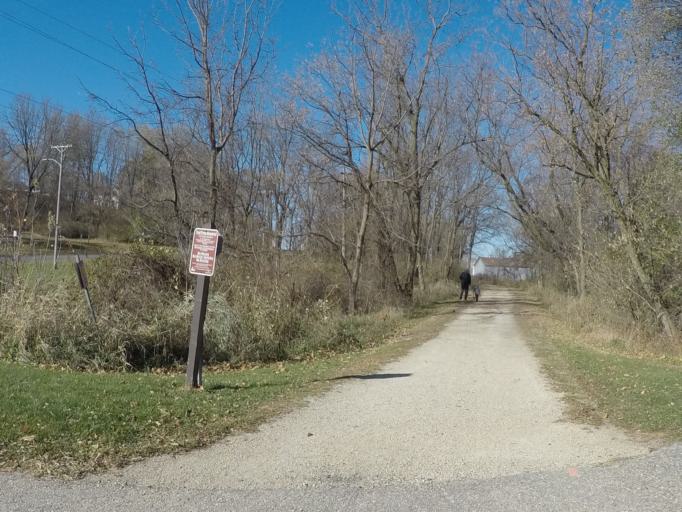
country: US
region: Wisconsin
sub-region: Dane County
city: Deerfield
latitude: 43.0541
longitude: -89.0704
